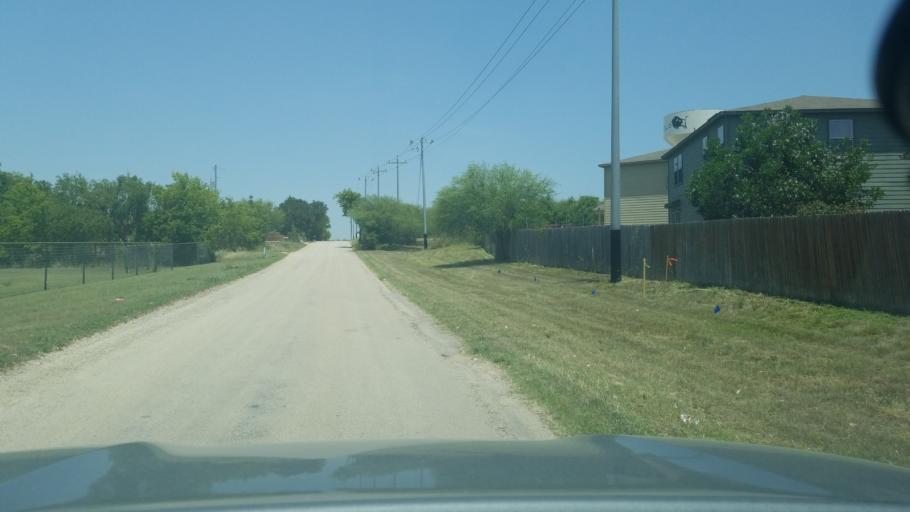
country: US
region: Texas
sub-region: Guadalupe County
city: Northcliff
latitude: 29.5959
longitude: -98.2235
